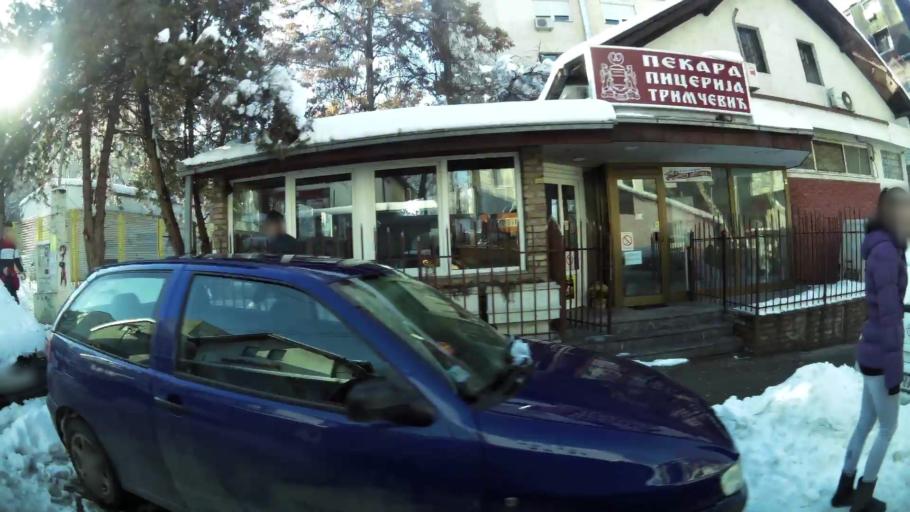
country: RS
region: Central Serbia
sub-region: Belgrade
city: Palilula
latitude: 44.8141
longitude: 20.5147
